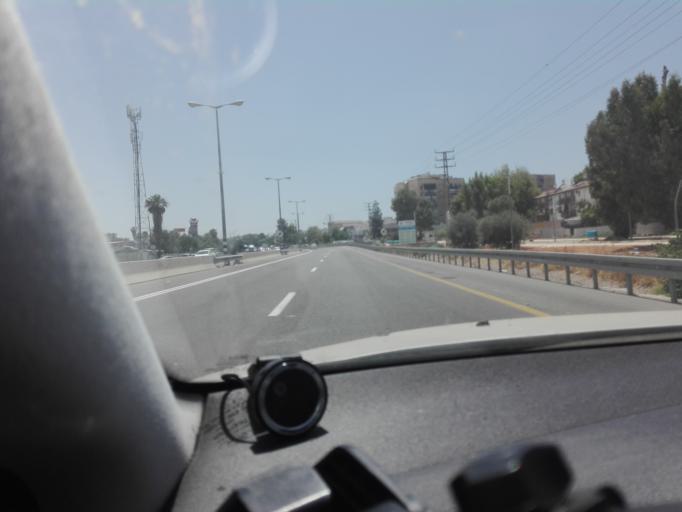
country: IL
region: Central District
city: Bene 'Ayish
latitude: 31.7293
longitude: 34.7518
